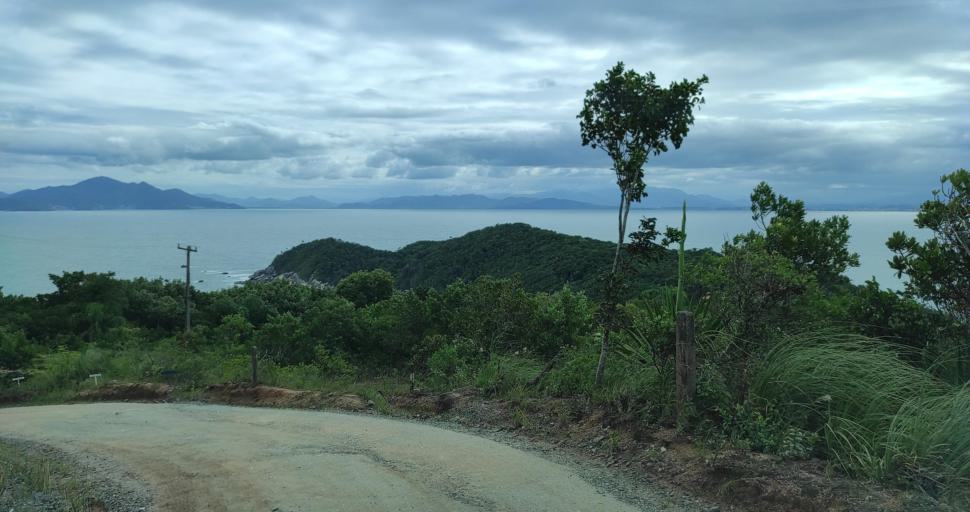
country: BR
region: Santa Catarina
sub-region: Porto Belo
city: Porto Belo
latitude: -27.2136
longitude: -48.5066
